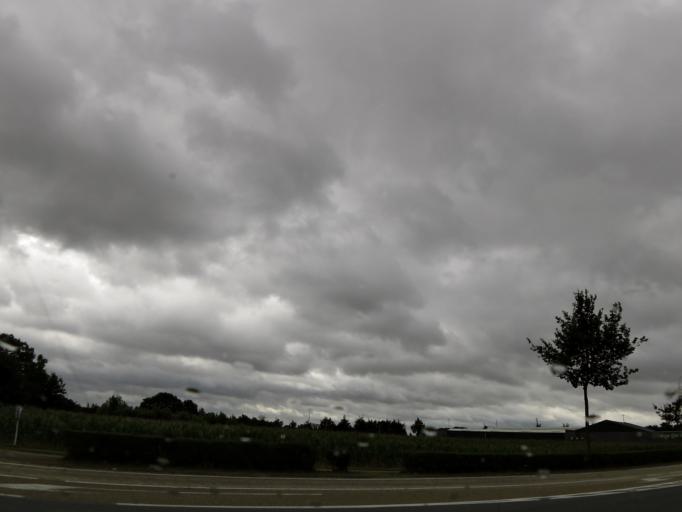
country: BE
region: Flanders
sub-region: Provincie Limburg
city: Maaseik
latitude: 51.0899
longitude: 5.7681
